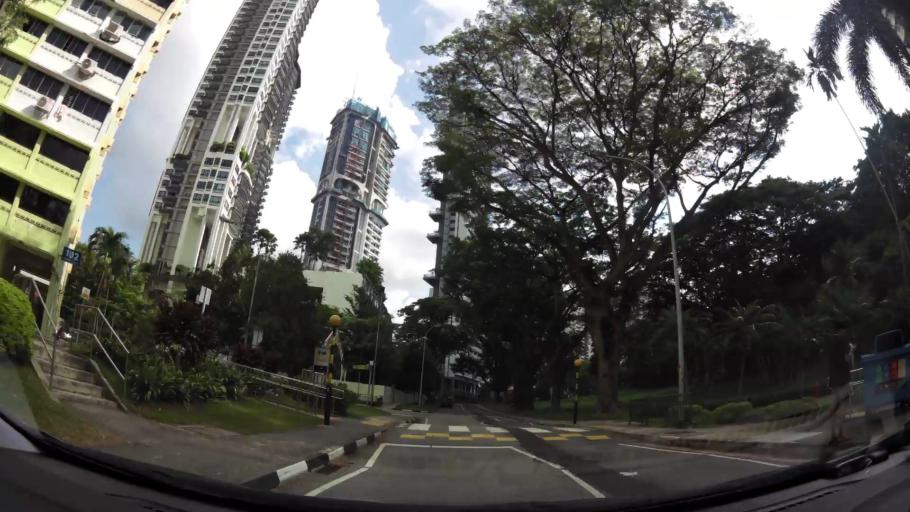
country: SG
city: Singapore
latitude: 1.2745
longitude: 103.8364
